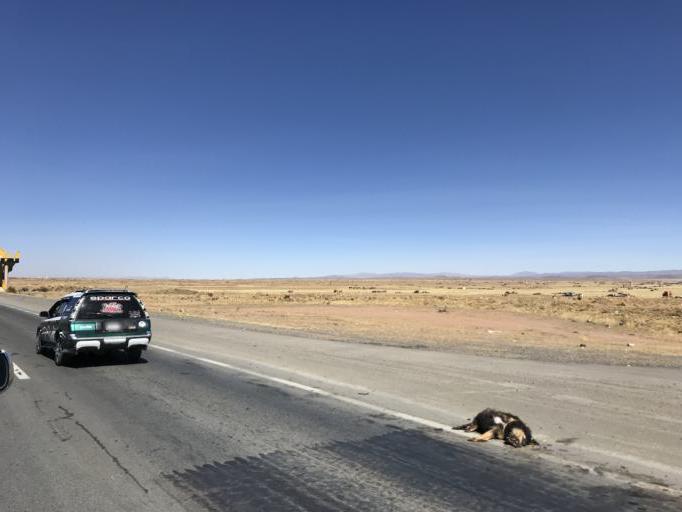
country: BO
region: La Paz
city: Batallas
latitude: -16.4042
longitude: -68.3557
